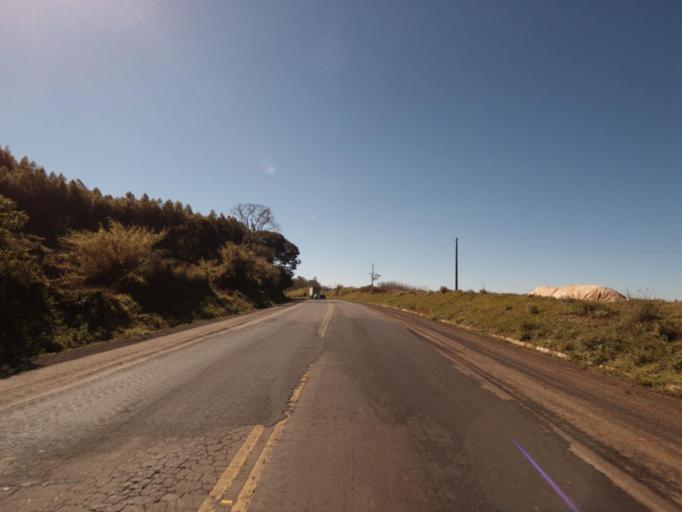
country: BR
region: Rio Grande do Sul
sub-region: Frederico Westphalen
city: Frederico Westphalen
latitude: -26.9163
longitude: -53.1902
